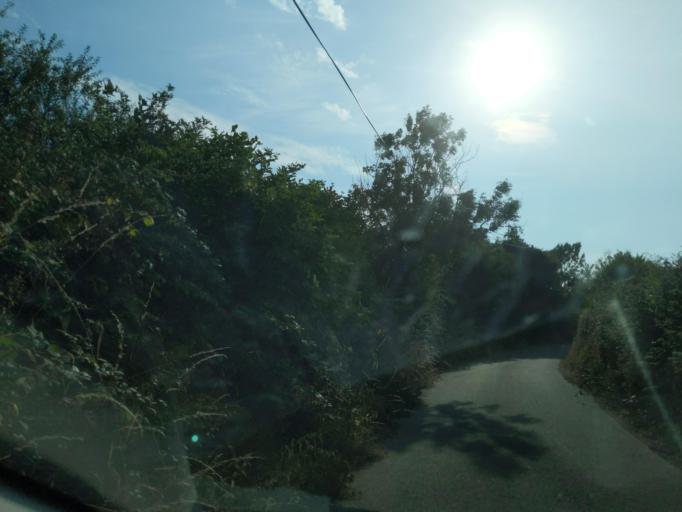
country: GB
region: England
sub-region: Devon
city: Winkleigh
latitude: 50.9654
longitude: -3.9872
